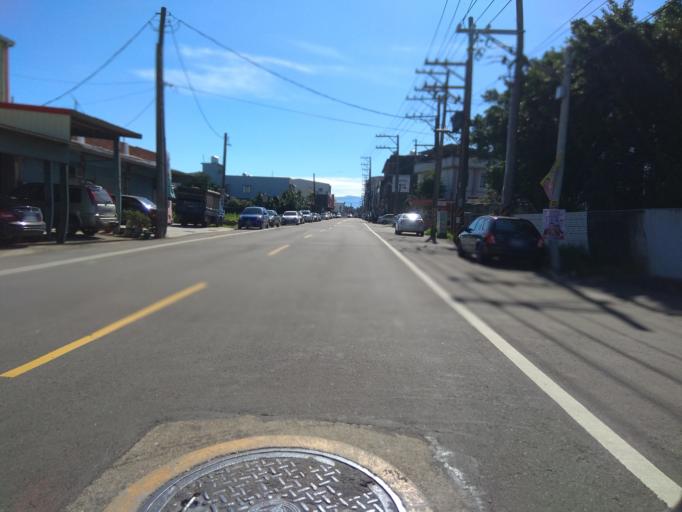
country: TW
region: Taiwan
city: Taoyuan City
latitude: 24.9762
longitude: 121.1372
